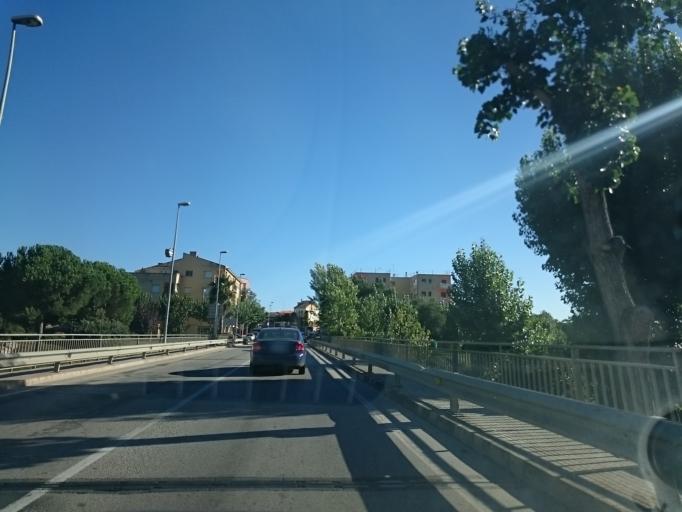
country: ES
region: Catalonia
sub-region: Provincia de Barcelona
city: Piera
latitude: 41.5259
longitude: 1.7498
